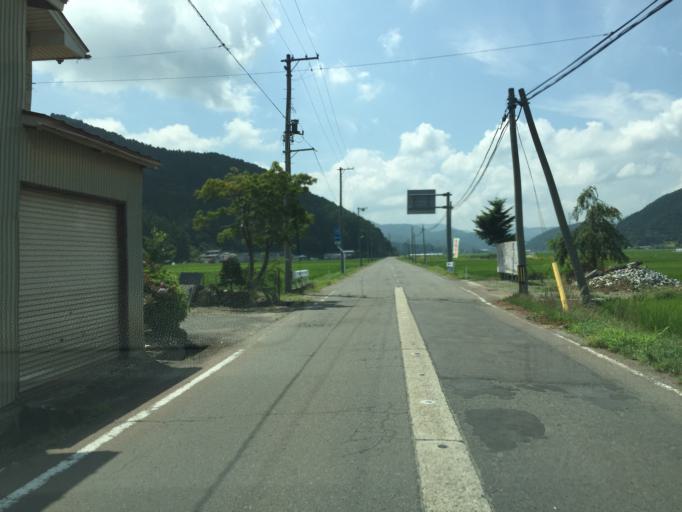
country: JP
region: Fukushima
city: Inawashiro
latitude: 37.4148
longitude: 140.0847
